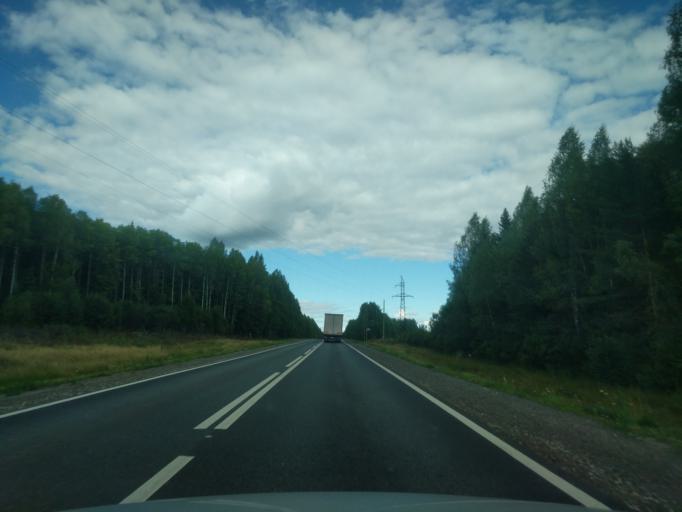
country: RU
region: Kostroma
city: Kadyy
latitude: 57.8456
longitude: 43.4607
